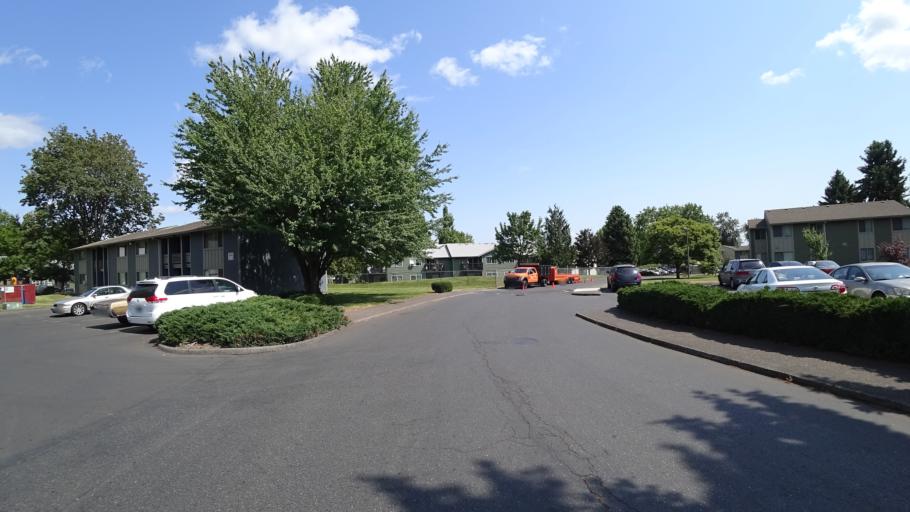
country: US
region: Oregon
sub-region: Washington County
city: West Haven
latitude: 45.6011
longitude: -122.7496
